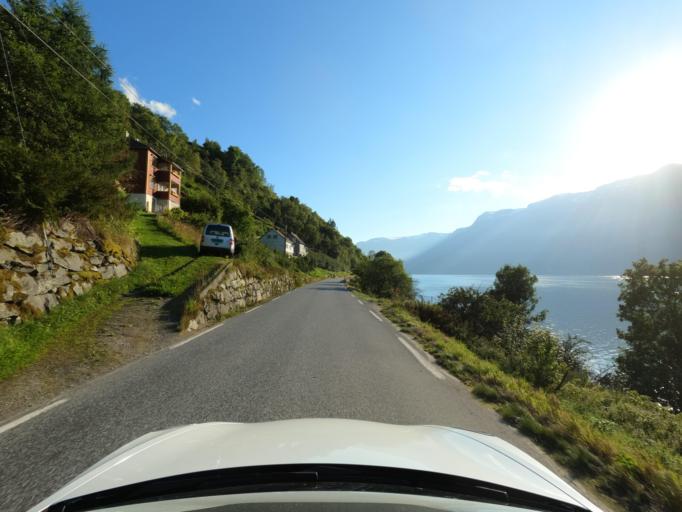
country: NO
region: Hordaland
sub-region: Ullensvang
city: Kinsarvik
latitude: 60.3134
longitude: 6.6523
